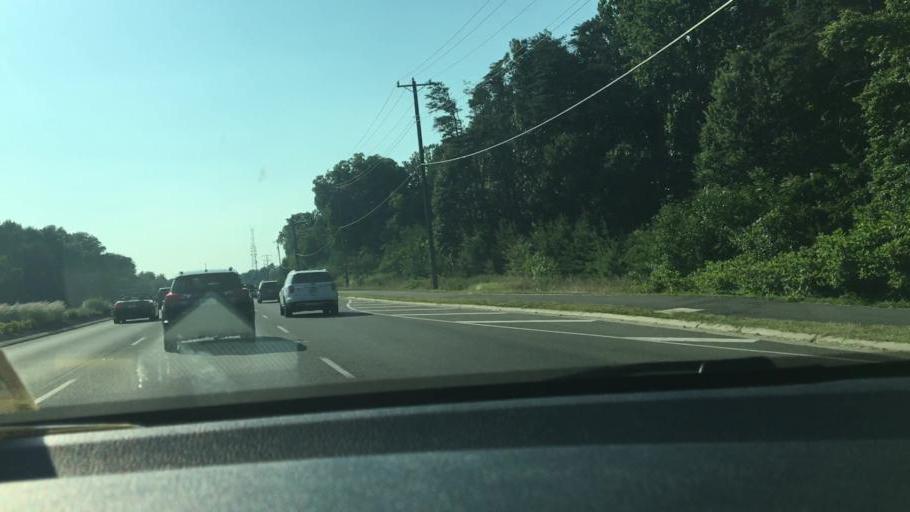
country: US
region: Virginia
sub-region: Prince William County
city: Lake Ridge
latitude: 38.6749
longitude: -77.3411
